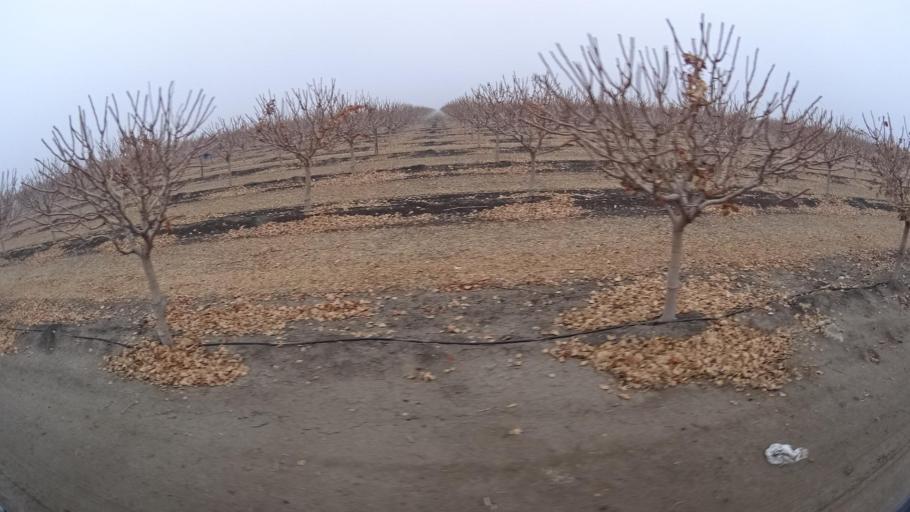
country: US
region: California
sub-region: Kern County
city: Buttonwillow
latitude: 35.4586
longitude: -119.5649
